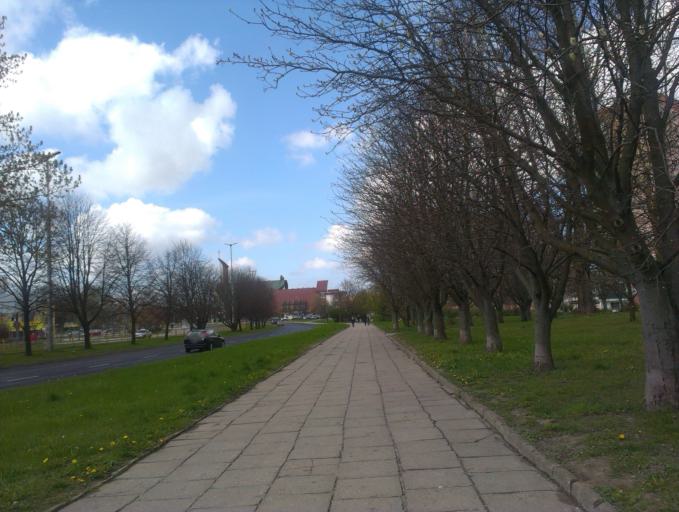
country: PL
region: West Pomeranian Voivodeship
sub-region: Koszalin
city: Koszalin
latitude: 54.2043
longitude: 16.1947
